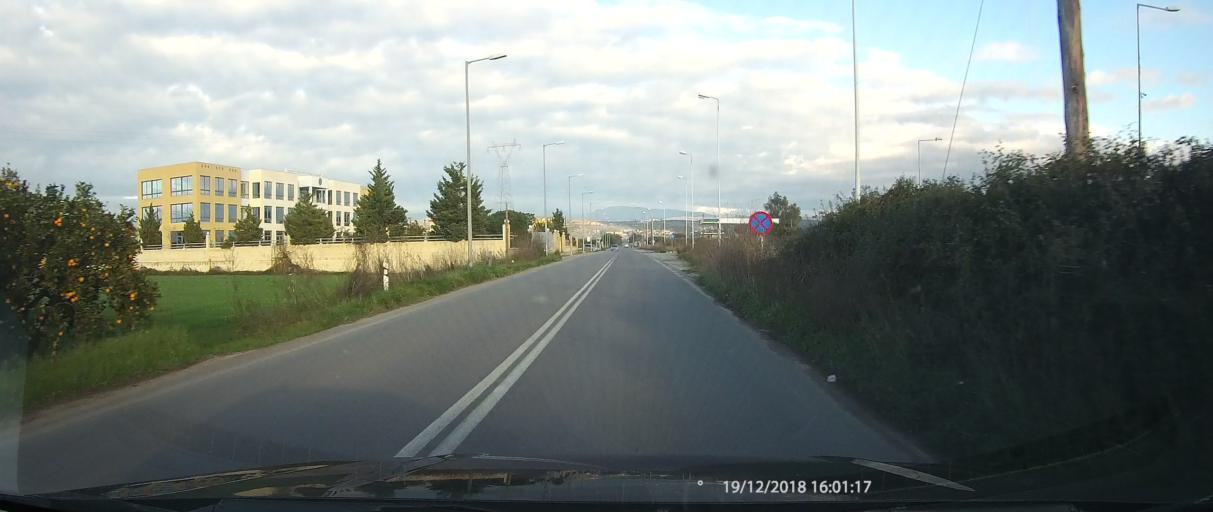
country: GR
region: Peloponnese
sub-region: Nomos Lakonias
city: Vlakhiotis
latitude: 36.8562
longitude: 22.6862
